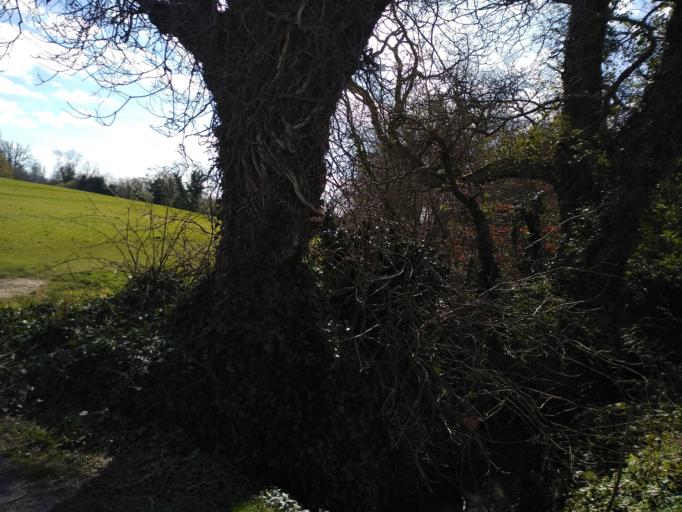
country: IE
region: Leinster
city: Malahide
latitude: 53.4422
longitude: -6.1707
